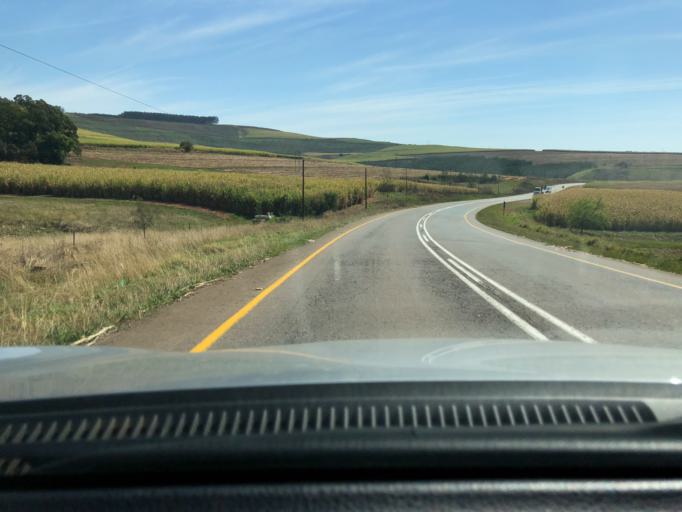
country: ZA
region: KwaZulu-Natal
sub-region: uMgungundlovu District Municipality
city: Richmond
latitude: -29.8066
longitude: 30.3436
